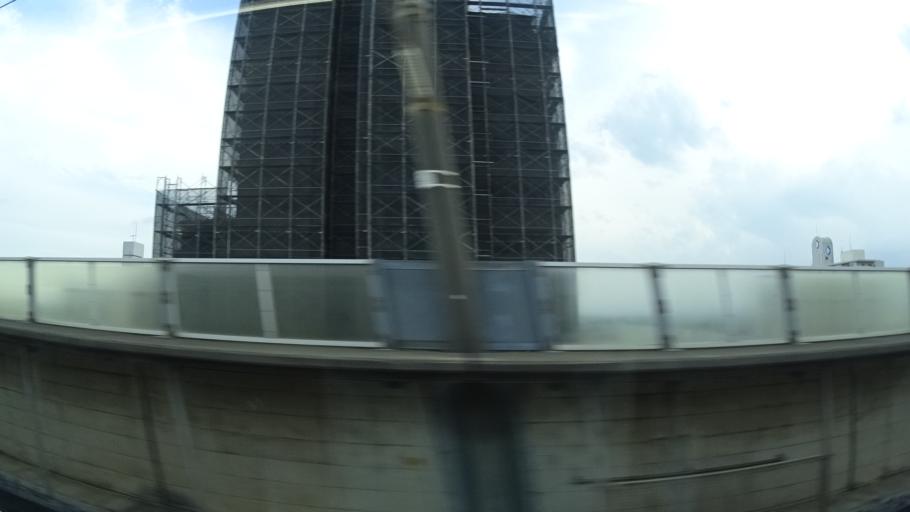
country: JP
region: Saitama
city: Kumagaya
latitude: 36.1427
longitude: 139.3809
